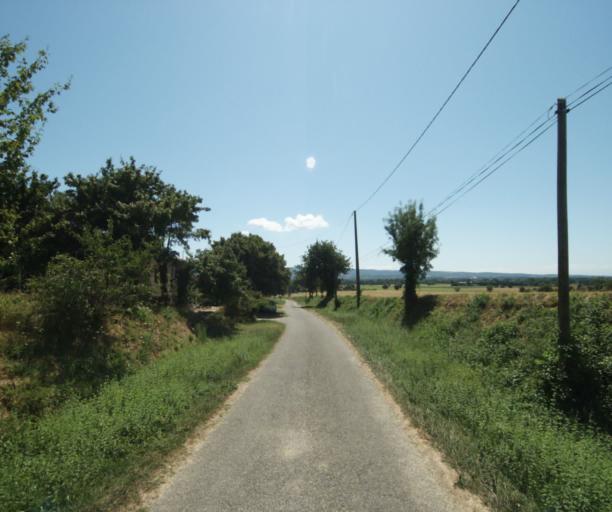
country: FR
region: Midi-Pyrenees
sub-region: Departement de la Haute-Garonne
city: Saint-Felix-Lauragais
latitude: 43.4939
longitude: 1.9416
